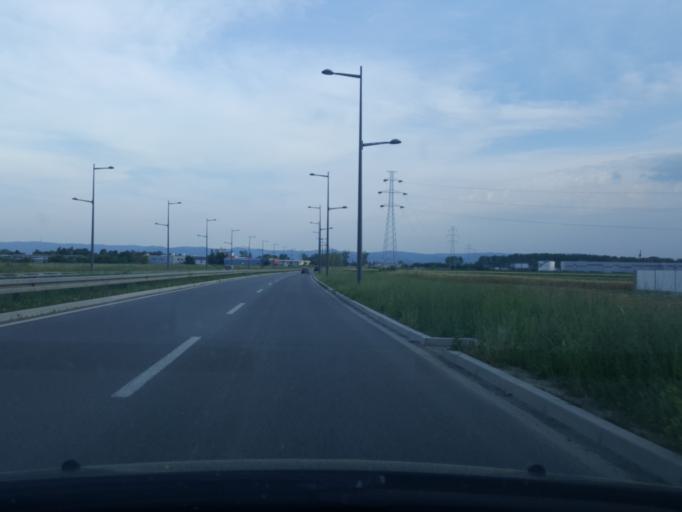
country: RS
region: Autonomna Pokrajina Vojvodina
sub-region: Juznobacki Okrug
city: Novi Sad
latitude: 45.2942
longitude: 19.8077
